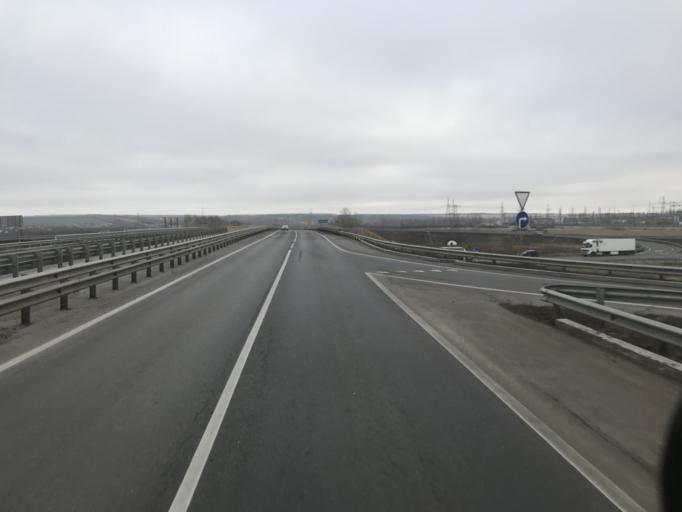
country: RU
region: Penza
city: Bogoslovka
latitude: 53.1305
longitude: 44.7777
